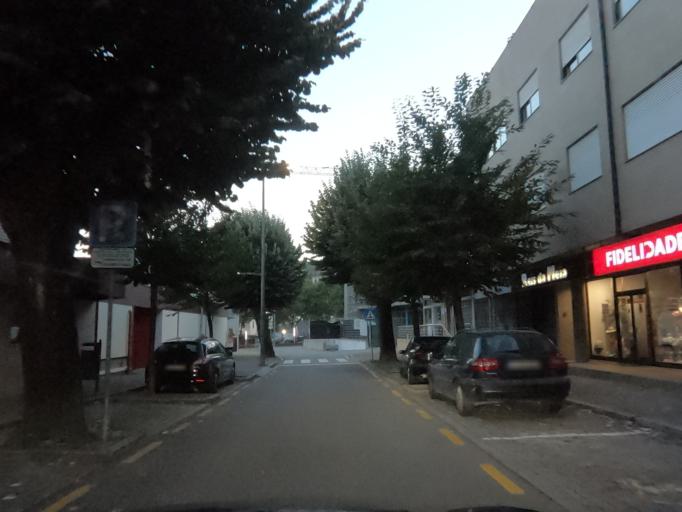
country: PT
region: Porto
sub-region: Valongo
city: Valongo
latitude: 41.1906
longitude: -8.4985
